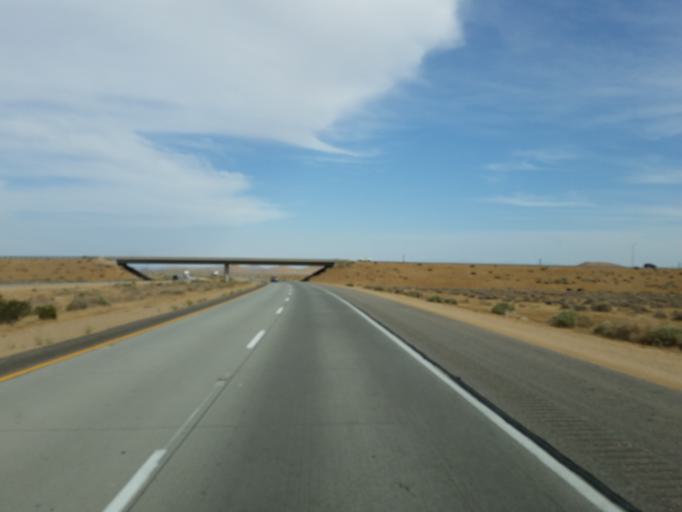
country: US
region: California
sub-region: Kern County
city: Mojave
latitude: 35.0401
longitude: -118.1092
